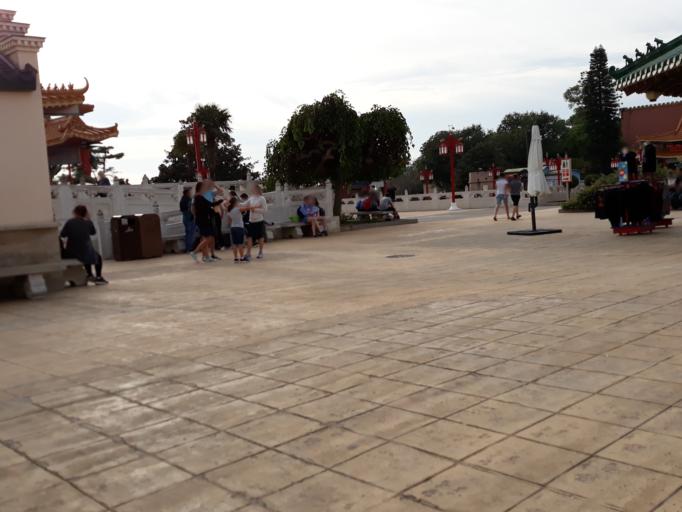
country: ES
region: Catalonia
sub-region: Provincia de Tarragona
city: Salou
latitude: 41.0887
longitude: 1.1612
